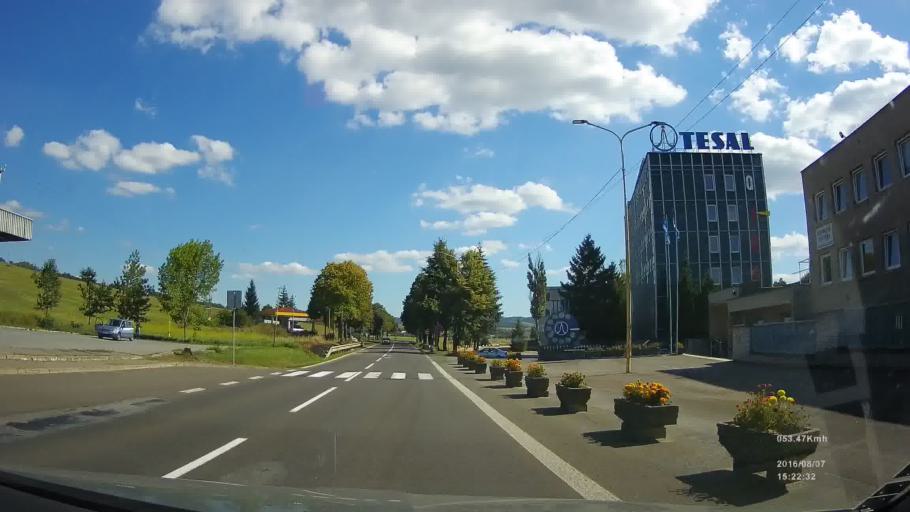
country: SK
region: Presovsky
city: Stropkov
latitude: 49.1918
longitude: 21.6564
